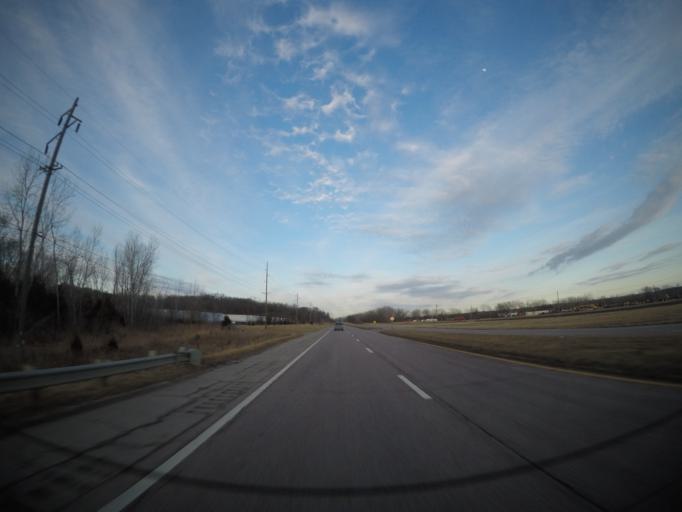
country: US
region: Kansas
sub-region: Wyandotte County
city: Edwardsville
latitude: 39.0680
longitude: -94.7702
